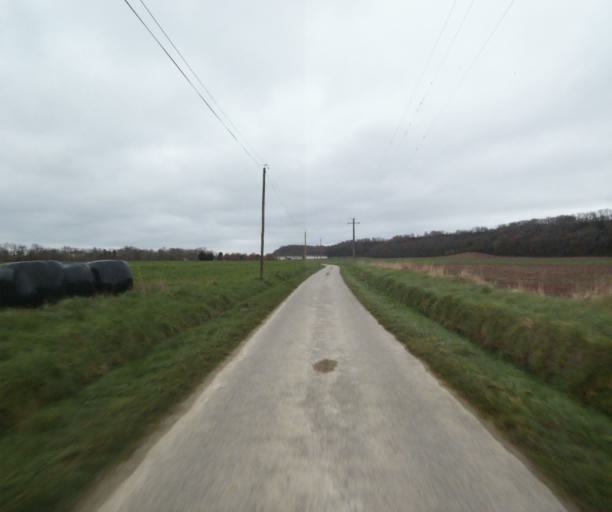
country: FR
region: Midi-Pyrenees
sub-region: Departement de l'Ariege
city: Saverdun
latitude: 43.2162
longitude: 1.5929
